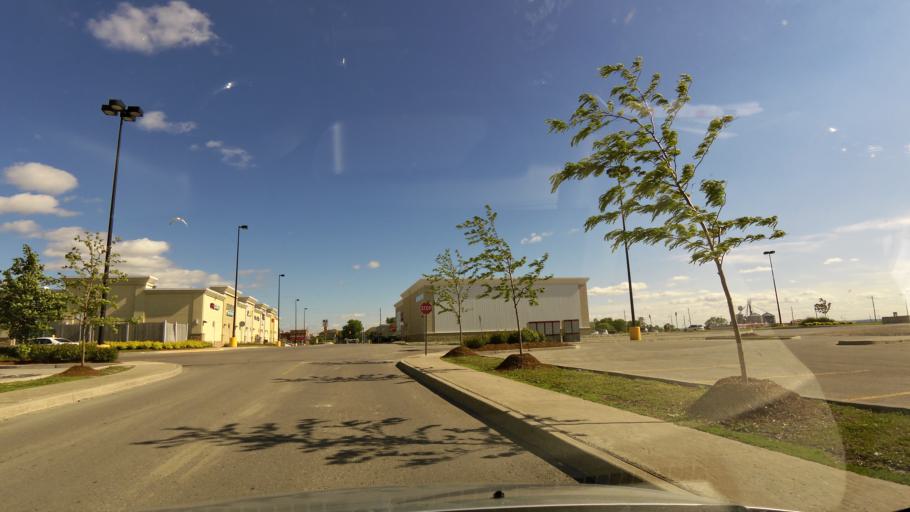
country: CA
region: Ontario
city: Bradford West Gwillimbury
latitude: 44.1088
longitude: -79.5988
